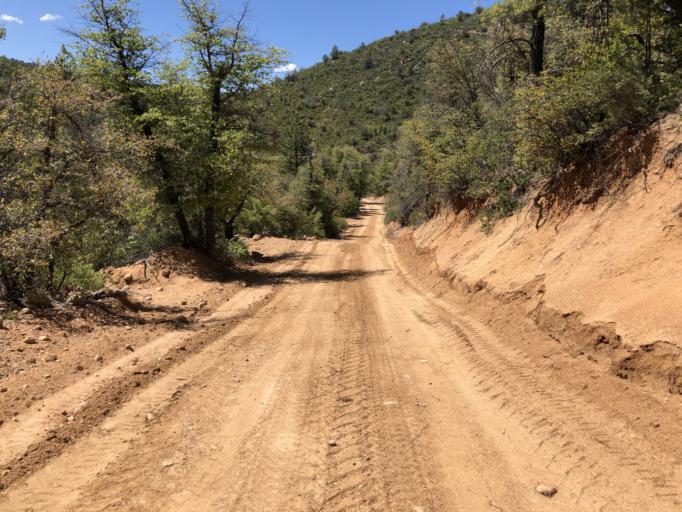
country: US
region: Arizona
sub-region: Gila County
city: Star Valley
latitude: 34.3512
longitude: -111.2766
